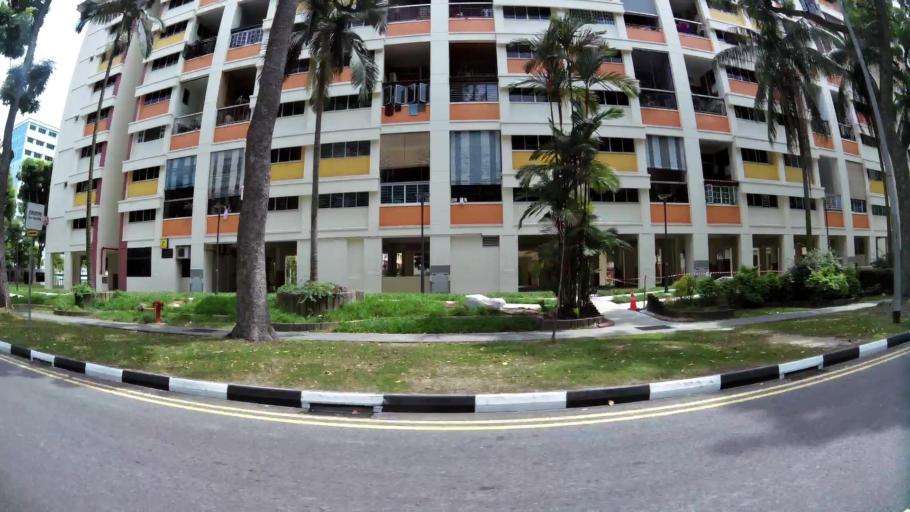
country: MY
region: Johor
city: Johor Bahru
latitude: 1.3461
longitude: 103.6969
